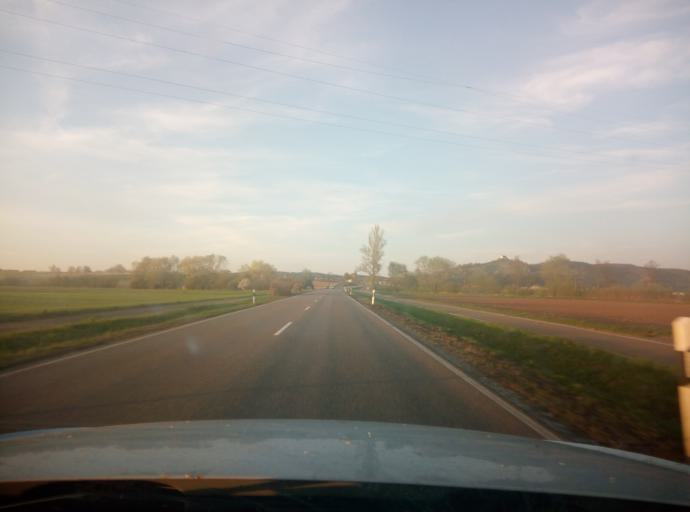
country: DE
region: Baden-Wuerttemberg
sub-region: Tuebingen Region
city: Rottenburg
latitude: 48.4953
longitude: 8.9585
